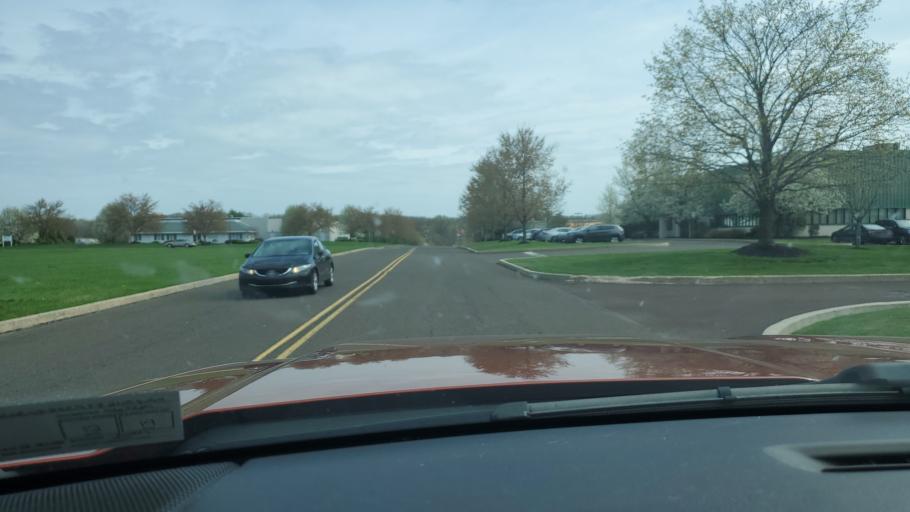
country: US
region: Pennsylvania
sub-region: Montgomery County
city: Hatfield
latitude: 40.2862
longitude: -75.2798
